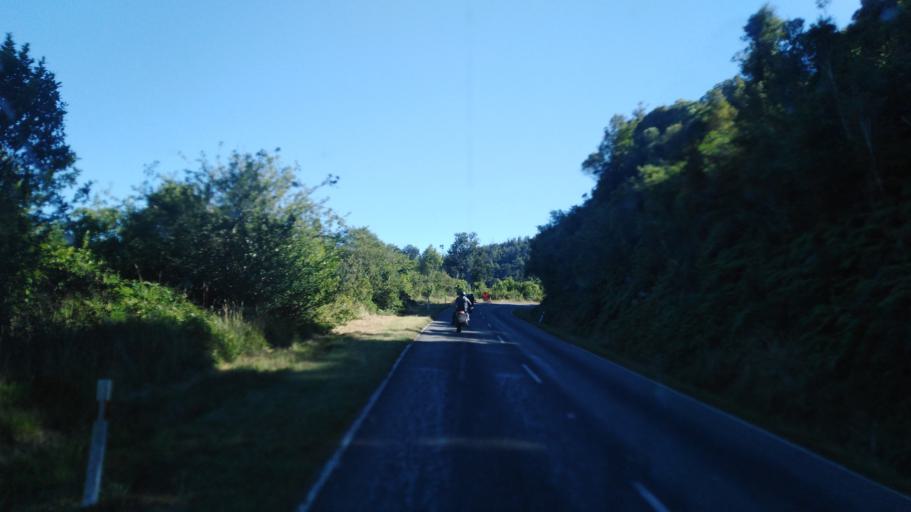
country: NZ
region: West Coast
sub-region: Buller District
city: Westport
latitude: -41.5331
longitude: 171.9926
